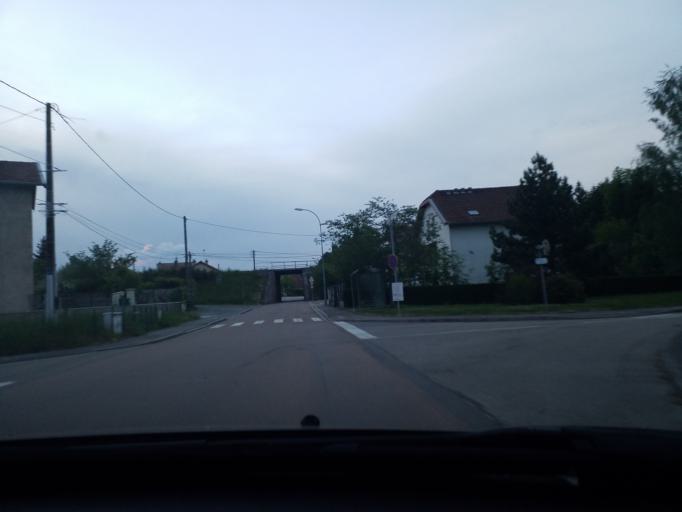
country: FR
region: Lorraine
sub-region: Departement des Vosges
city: Vittel
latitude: 48.2051
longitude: 5.9535
